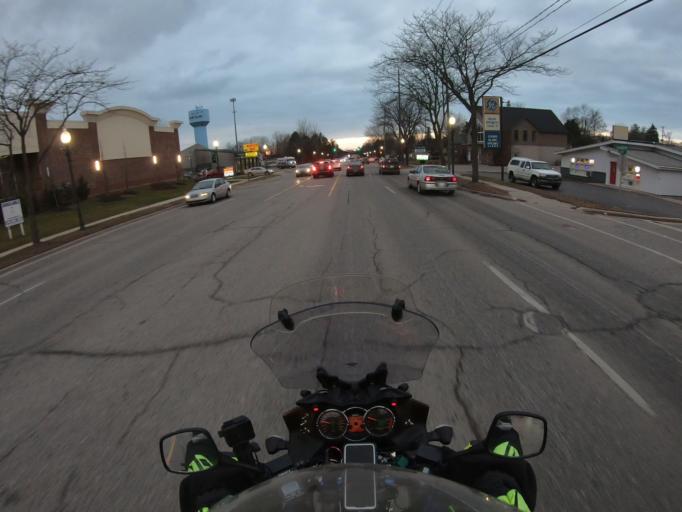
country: US
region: Michigan
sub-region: Genesee County
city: Grand Blanc
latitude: 42.9303
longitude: -83.6332
